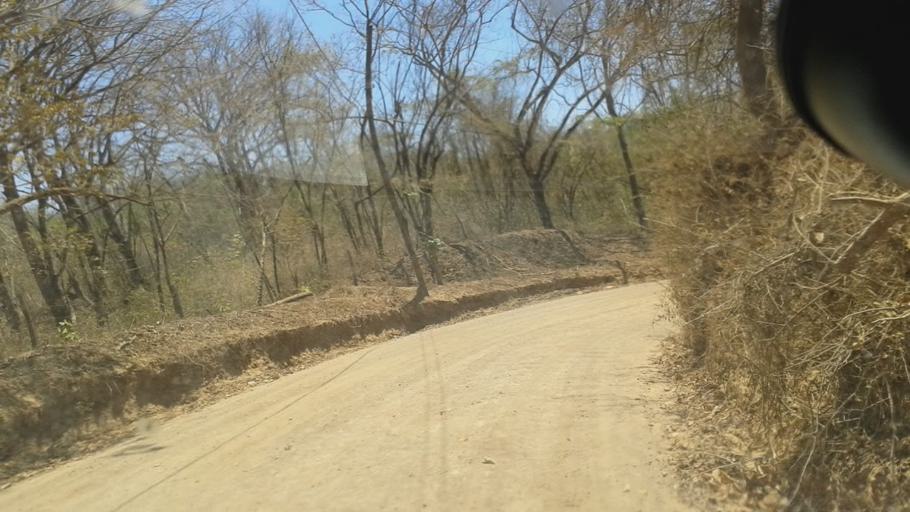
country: CR
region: Guanacaste
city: Samara
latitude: 10.0217
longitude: -85.7189
